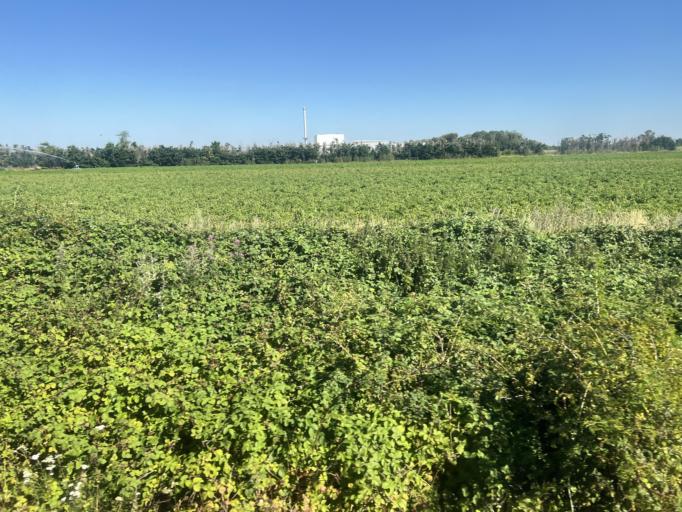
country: GB
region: England
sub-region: Lincolnshire
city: Sleaford
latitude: 52.9938
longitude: -0.3840
